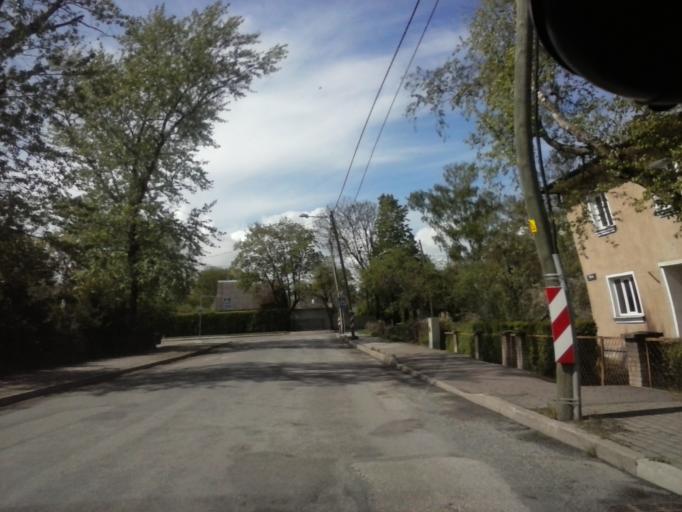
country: EE
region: Tartu
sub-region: Tartu linn
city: Tartu
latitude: 58.3619
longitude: 26.7241
